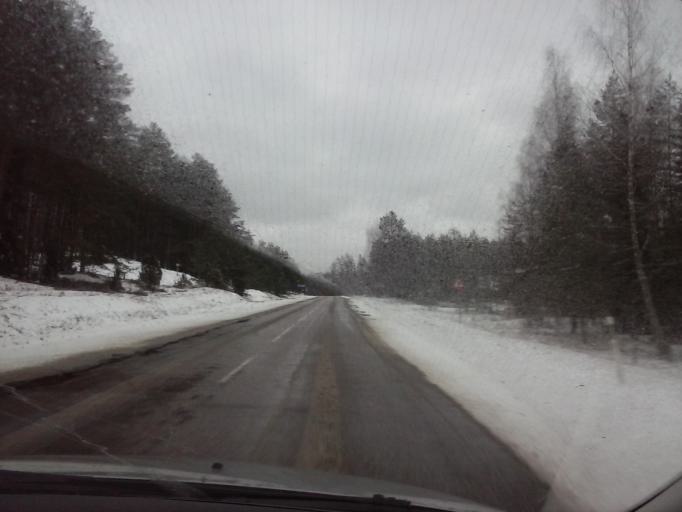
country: LV
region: Strenci
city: Seda
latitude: 57.6502
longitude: 25.8608
